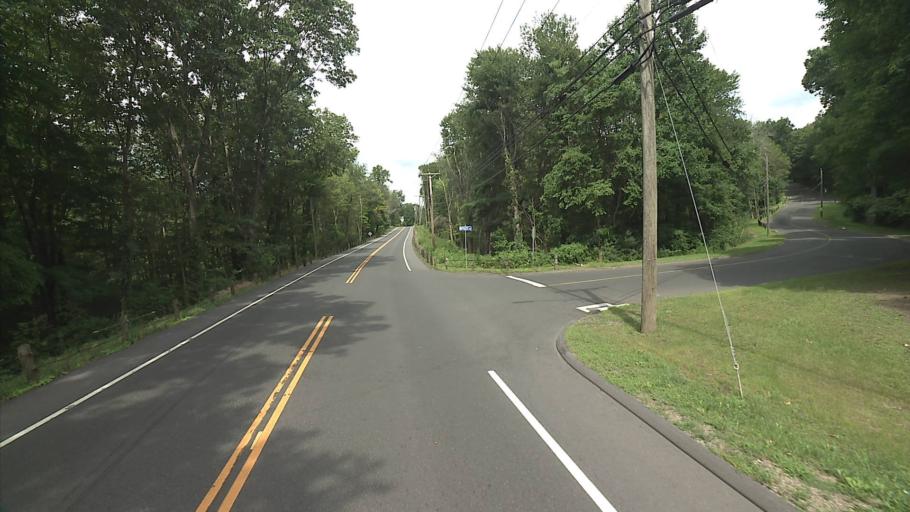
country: US
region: Connecticut
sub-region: New Haven County
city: Southbury
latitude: 41.4676
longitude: -73.1736
